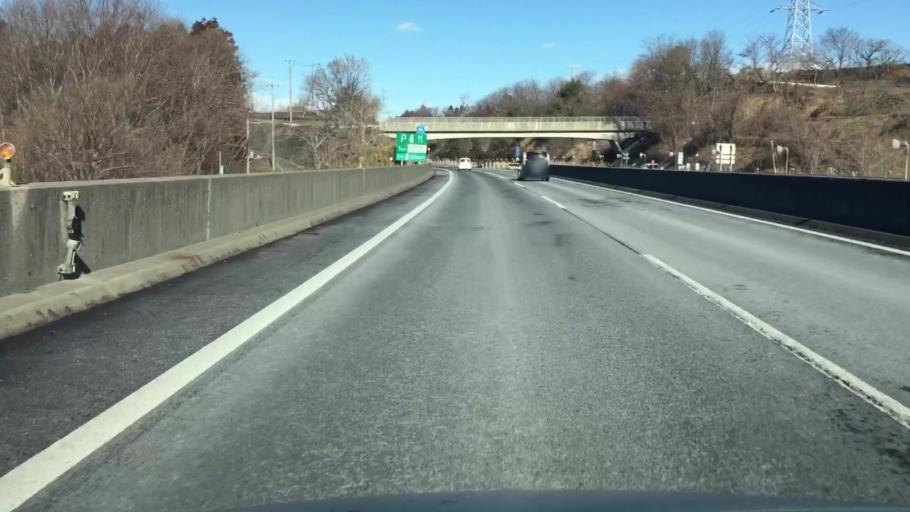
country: JP
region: Gunma
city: Numata
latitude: 36.5905
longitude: 139.0667
